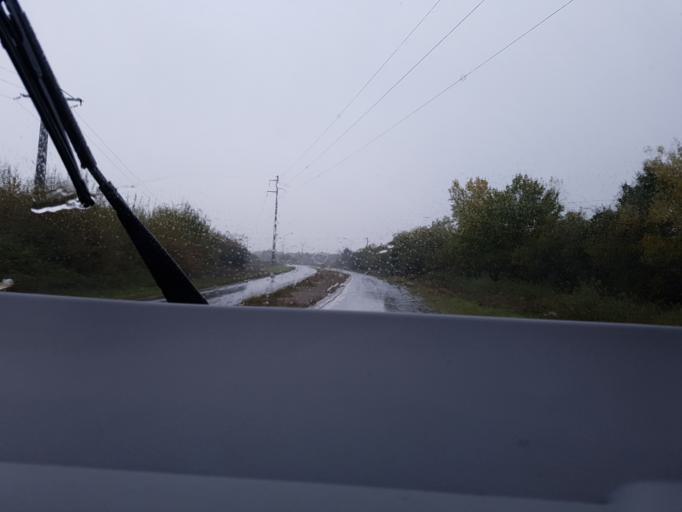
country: FR
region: Aquitaine
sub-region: Departement de la Gironde
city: Saint-Louis-de-Montferrand
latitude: 44.9526
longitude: -0.5182
